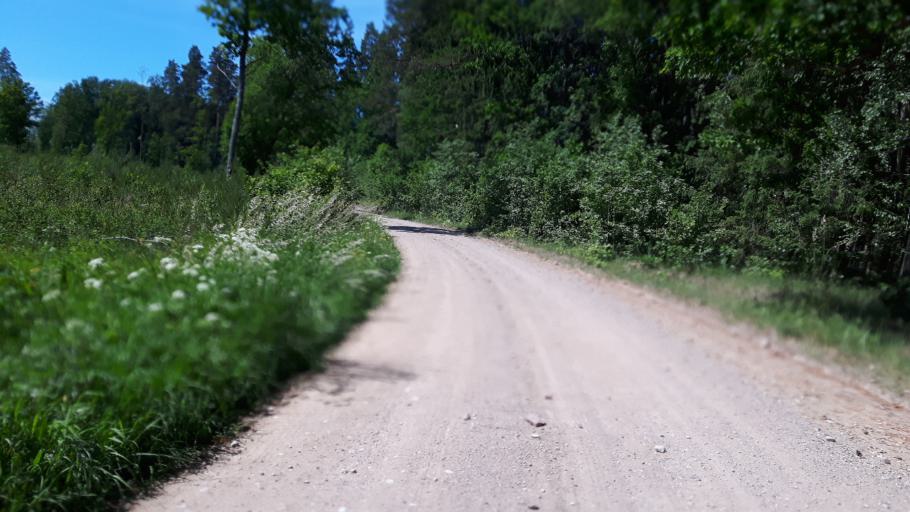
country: LV
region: Kandava
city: Kandava
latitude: 57.0429
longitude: 22.8439
